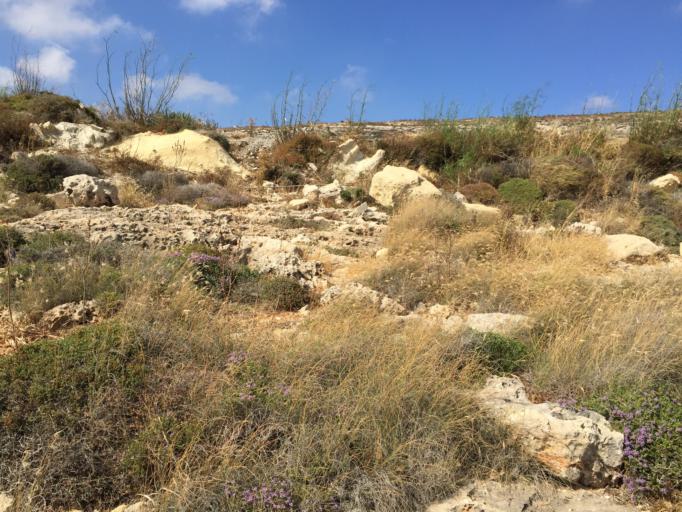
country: MT
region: Is-Siggiewi
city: Siggiewi
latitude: 35.8281
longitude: 14.4212
